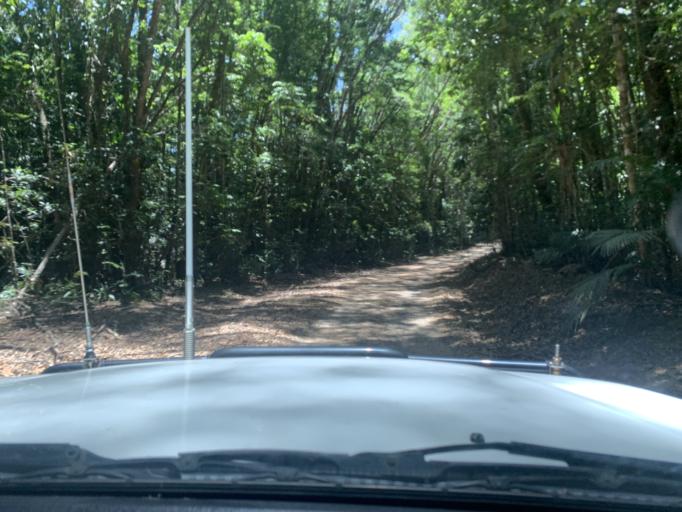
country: AU
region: Queensland
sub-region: Cairns
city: Redlynch
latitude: -16.9407
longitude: 145.6252
